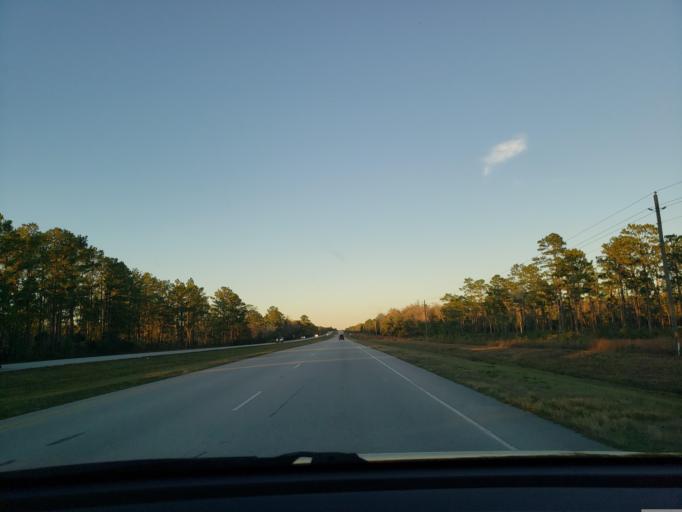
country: US
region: North Carolina
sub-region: Onslow County
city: Sneads Ferry
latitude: 34.6238
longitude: -77.4828
